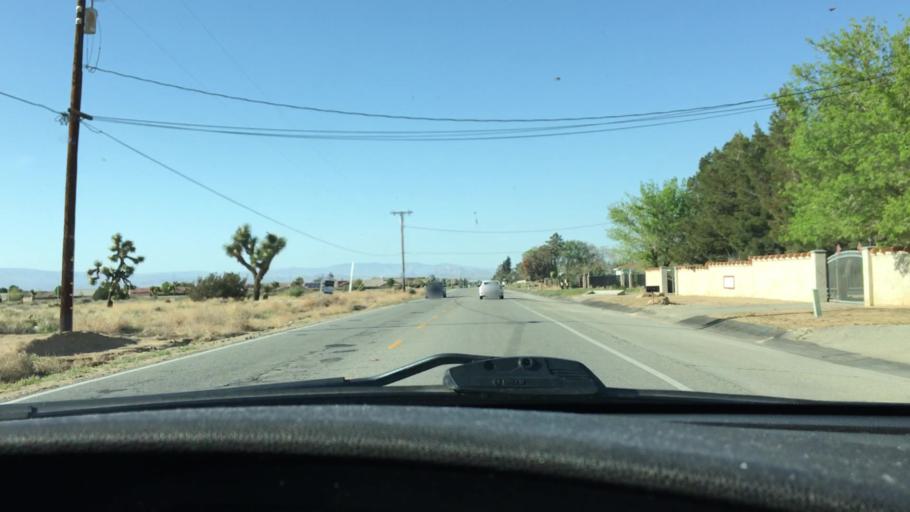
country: US
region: California
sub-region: Los Angeles County
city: Quartz Hill
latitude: 34.6356
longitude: -118.1833
